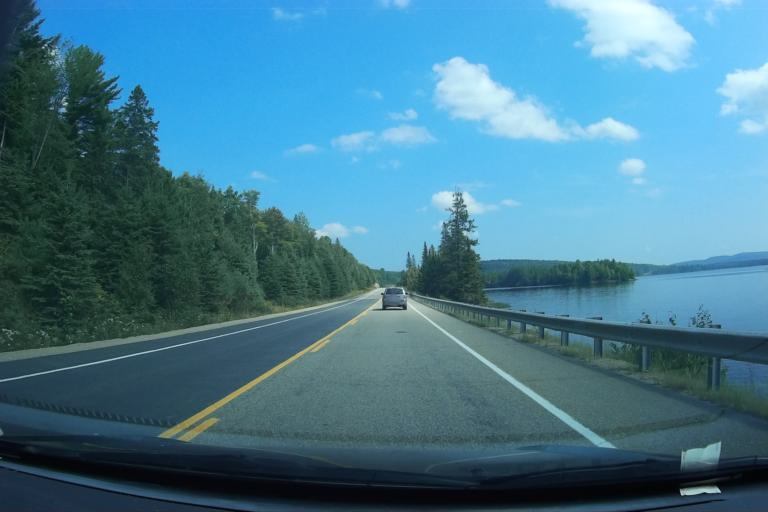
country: CA
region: Ontario
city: Huntsville
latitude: 45.5819
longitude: -78.4960
